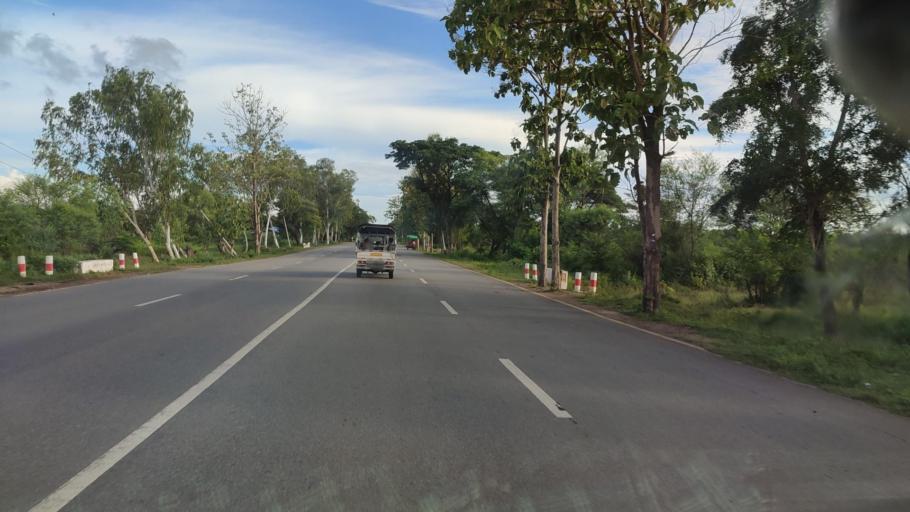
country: MM
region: Mandalay
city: Yamethin
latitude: 20.1651
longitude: 96.1899
